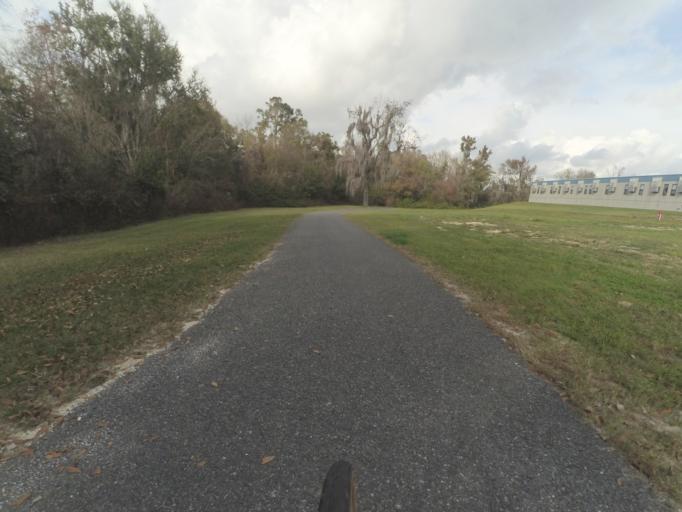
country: US
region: Florida
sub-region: Alachua County
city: Gainesville
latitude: 29.6365
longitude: -82.3543
